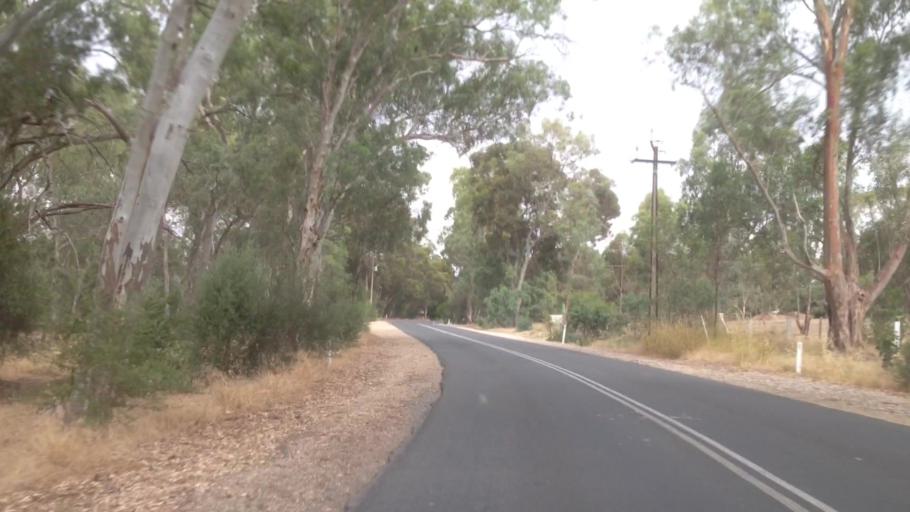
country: AU
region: South Australia
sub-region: Barossa
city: Williamstown
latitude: -34.6610
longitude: 138.8646
